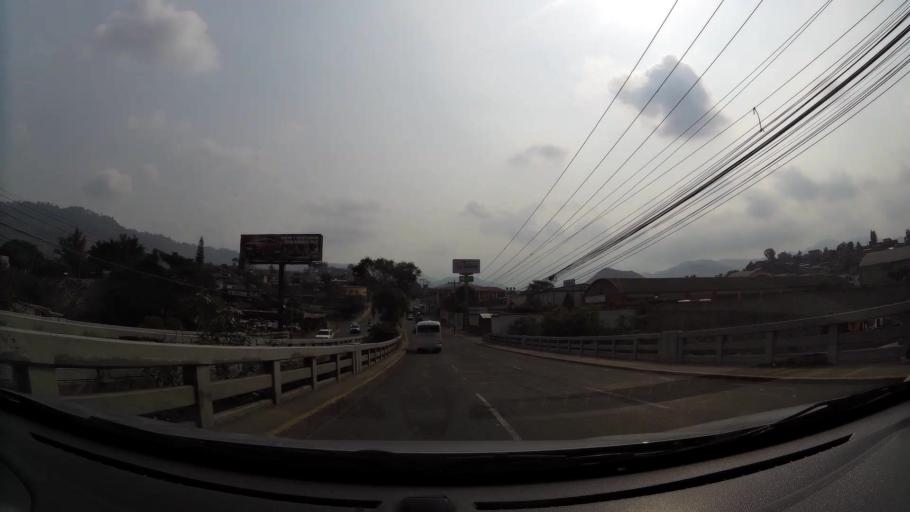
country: HN
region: Francisco Morazan
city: Tegucigalpa
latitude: 14.1036
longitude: -87.1750
